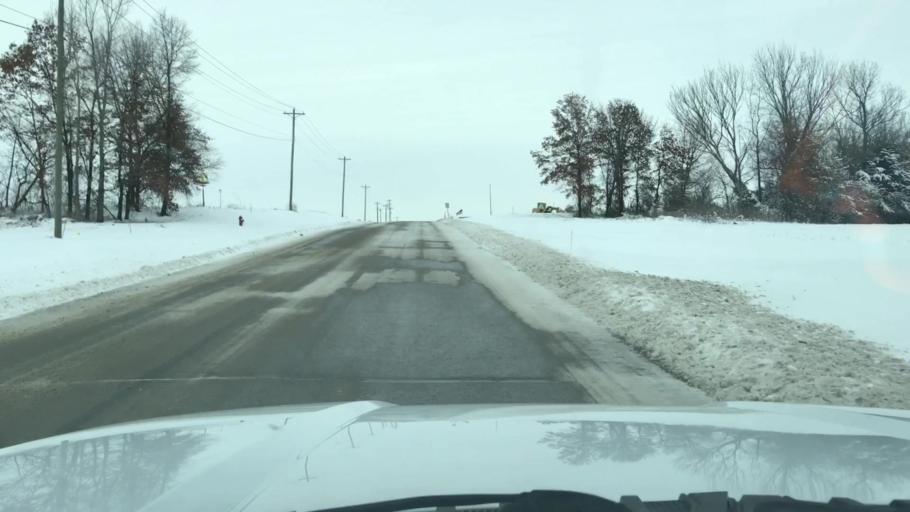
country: US
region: Missouri
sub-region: Clinton County
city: Cameron
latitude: 39.7485
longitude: -94.2153
